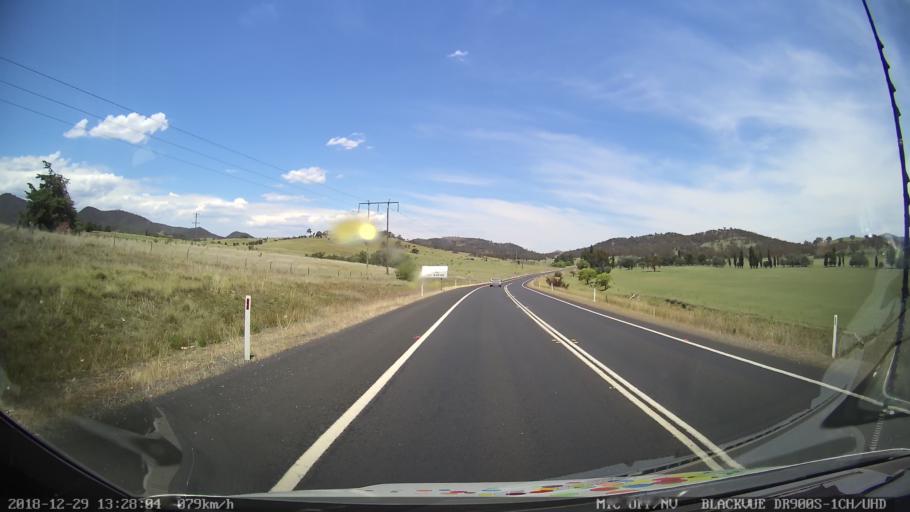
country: AU
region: New South Wales
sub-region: Cooma-Monaro
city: Cooma
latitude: -35.8706
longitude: 149.1612
